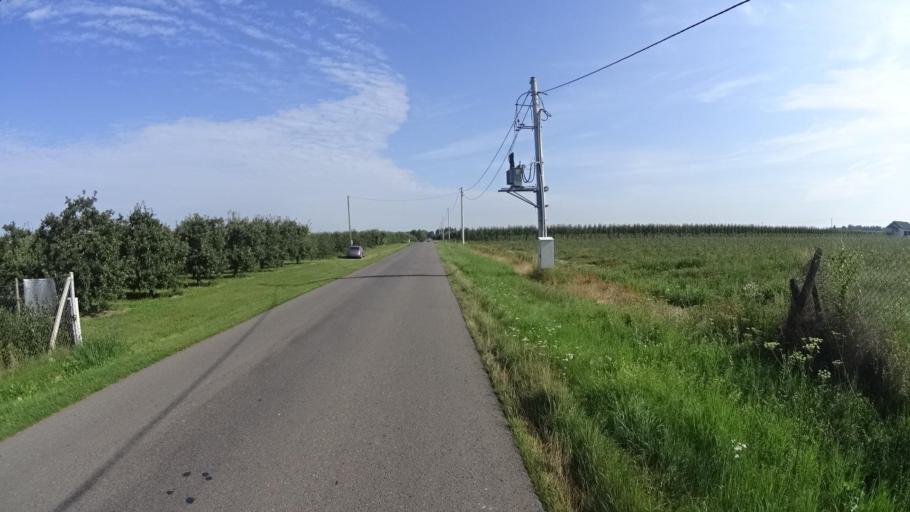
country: PL
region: Masovian Voivodeship
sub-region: Powiat grojecki
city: Goszczyn
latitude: 51.7580
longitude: 20.8530
